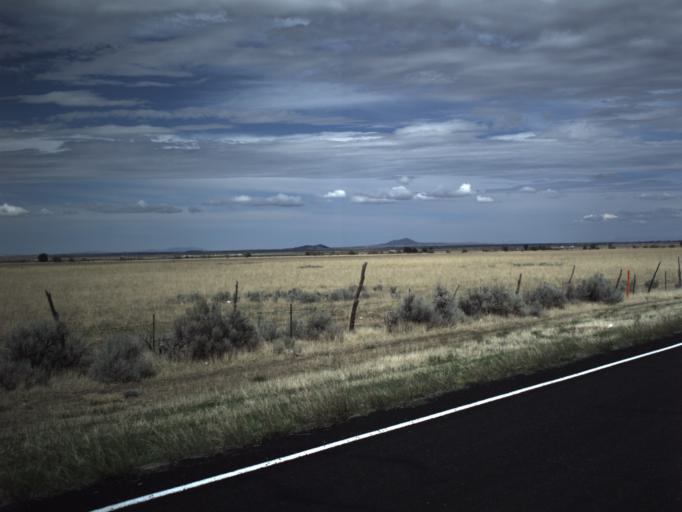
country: US
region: Utah
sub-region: Millard County
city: Fillmore
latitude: 38.8256
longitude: -112.4318
